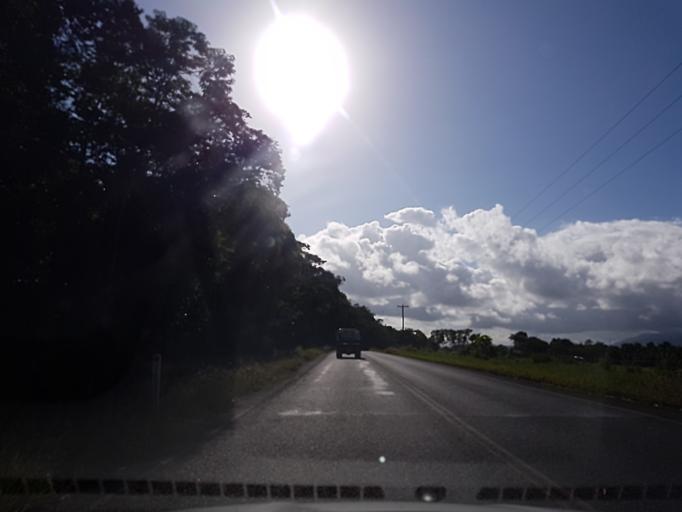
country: AU
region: Queensland
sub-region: Cairns
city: Port Douglas
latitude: -16.3204
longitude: 145.4063
